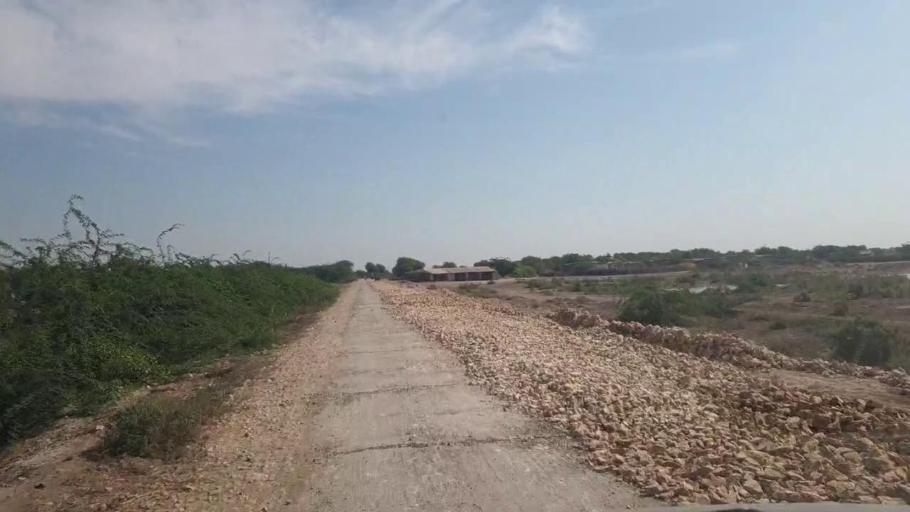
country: PK
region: Sindh
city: Tando Bago
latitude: 24.9427
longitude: 69.0982
